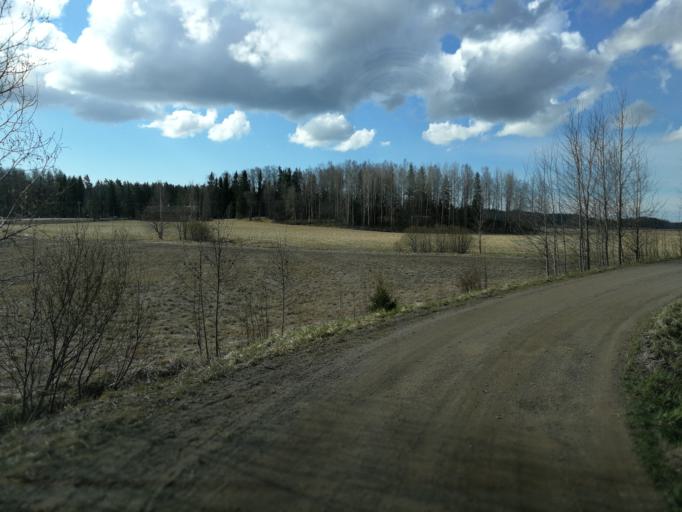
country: FI
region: Uusimaa
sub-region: Raaseporin
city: Inga
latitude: 60.1004
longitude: 23.9717
